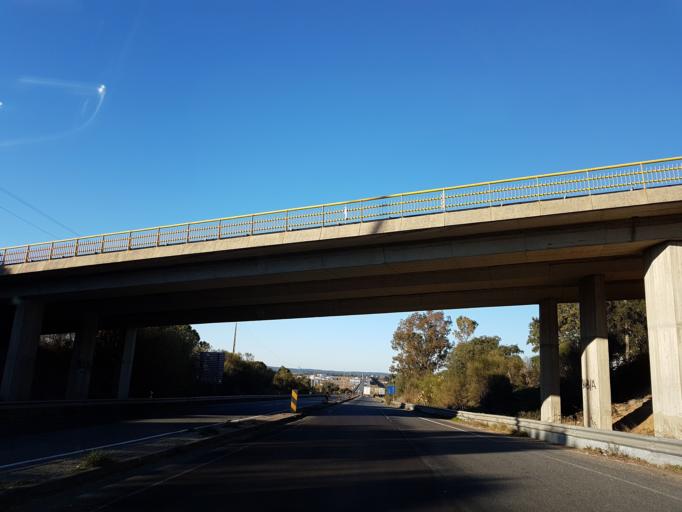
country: PT
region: Setubal
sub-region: Alcacer do Sal
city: Alcacer do Sal
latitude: 38.3608
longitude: -8.5218
